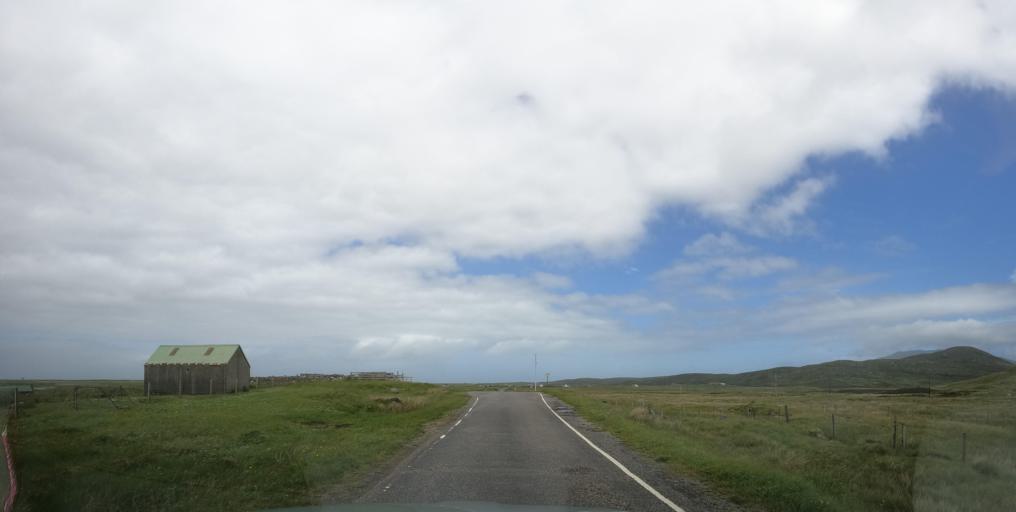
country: GB
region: Scotland
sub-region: Eilean Siar
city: Isle of South Uist
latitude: 57.2022
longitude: -7.3914
